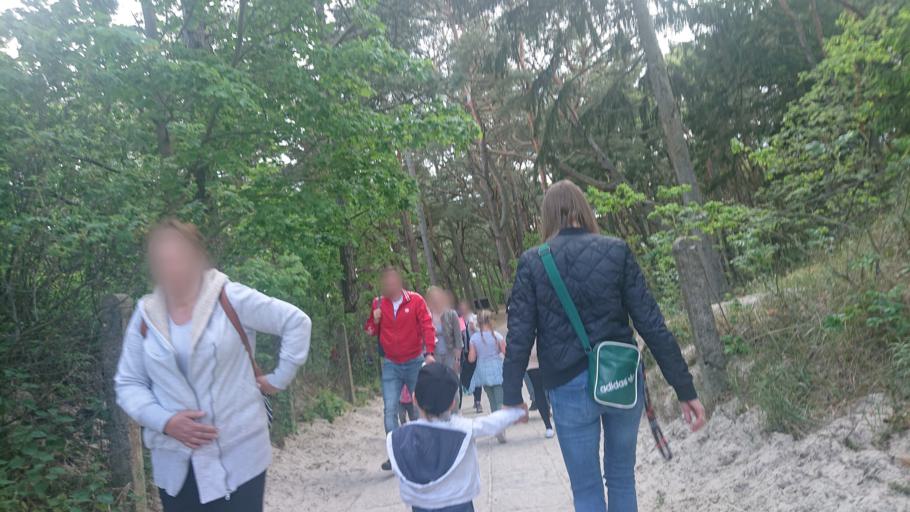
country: PL
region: Pomeranian Voivodeship
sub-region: Powiat pucki
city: Krokowa
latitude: 54.8321
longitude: 18.2126
